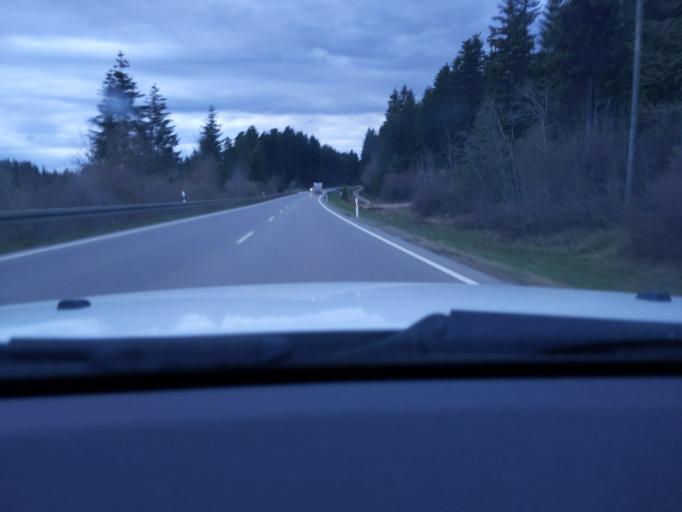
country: DE
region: Baden-Wuerttemberg
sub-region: Freiburg Region
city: Tuningen
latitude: 48.0445
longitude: 8.5668
